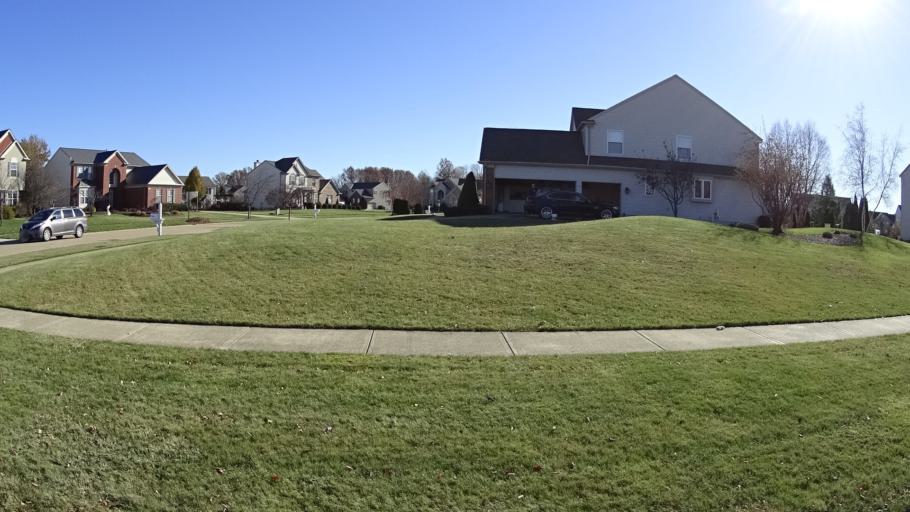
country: US
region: Ohio
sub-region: Lorain County
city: Avon
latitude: 41.4332
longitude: -82.0307
